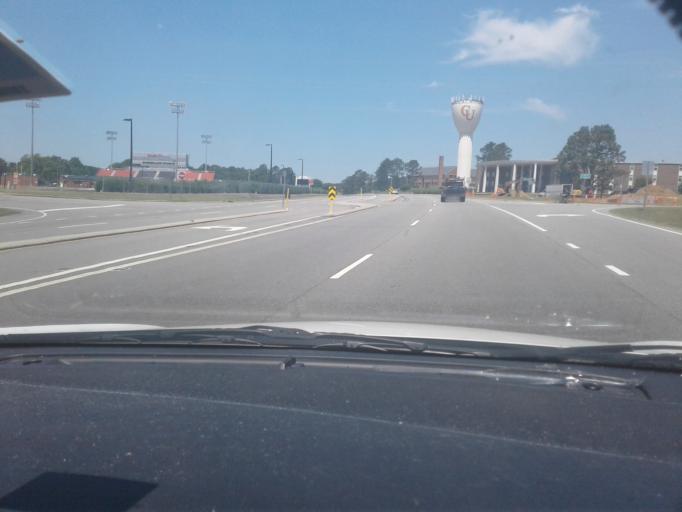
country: US
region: North Carolina
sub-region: Harnett County
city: Buies Creek
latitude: 35.4041
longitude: -78.7390
